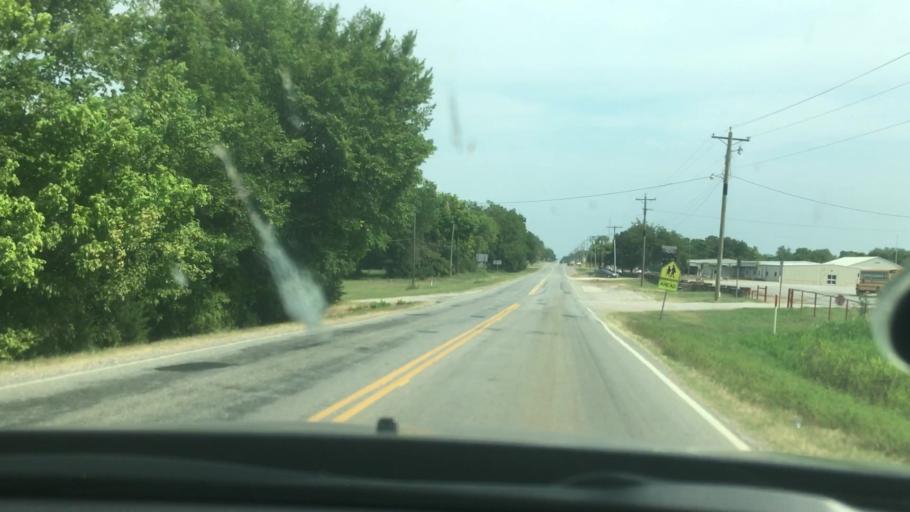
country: US
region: Oklahoma
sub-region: Coal County
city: Coalgate
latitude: 34.3684
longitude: -96.4245
